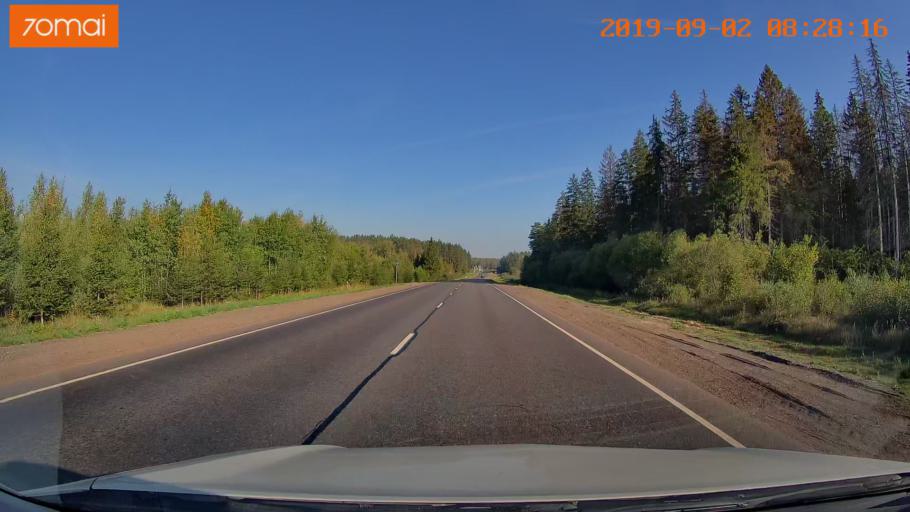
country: RU
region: Kaluga
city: Maloyaroslavets
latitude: 54.9918
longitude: 36.4012
